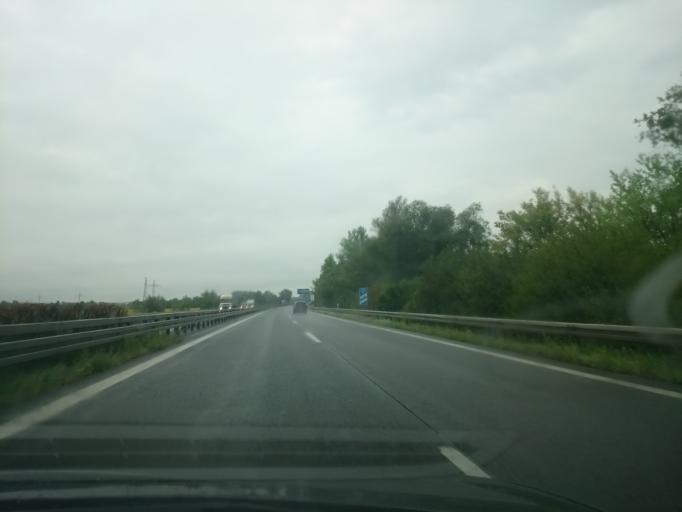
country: DE
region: Brandenburg
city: Brieselang
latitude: 52.5796
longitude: 12.9730
